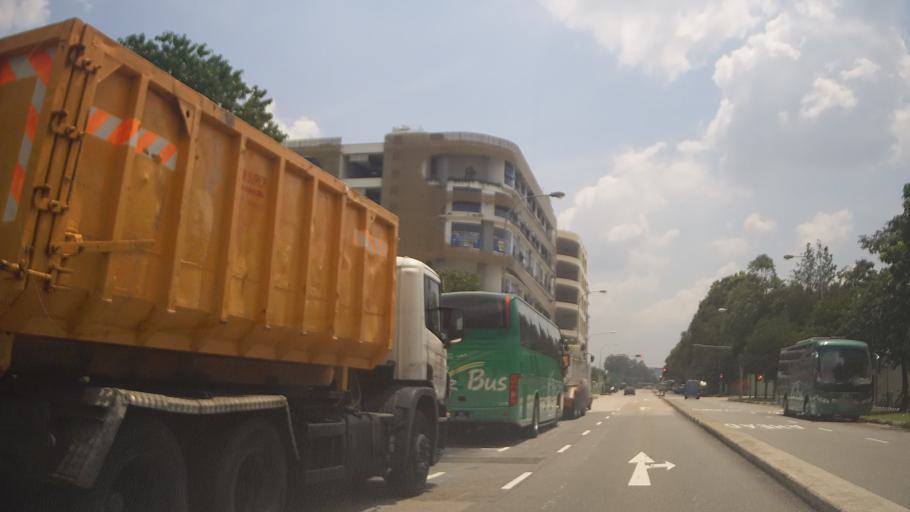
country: MY
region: Johor
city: Johor Bahru
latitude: 1.4506
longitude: 103.7998
